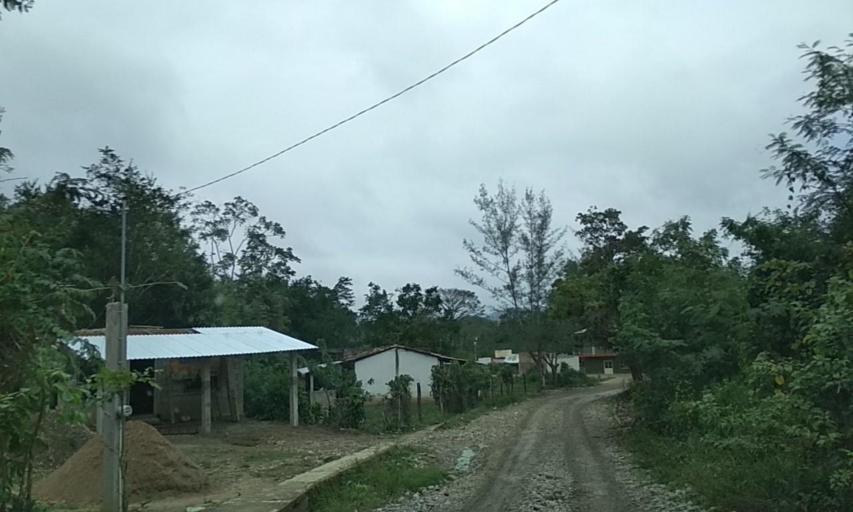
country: MX
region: Veracruz
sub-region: Papantla
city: El Chote
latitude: 20.3826
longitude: -97.3521
